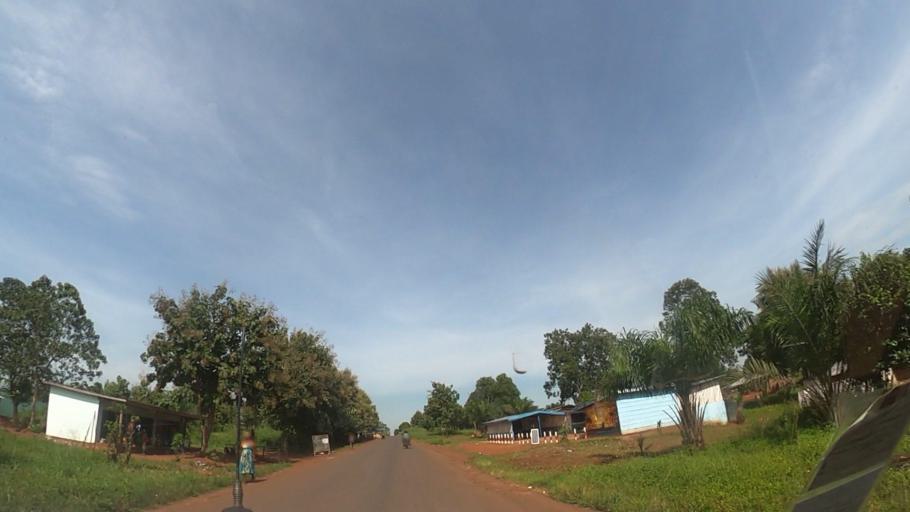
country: CF
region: Ombella-Mpoko
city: Bimbo
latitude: 4.3128
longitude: 18.4758
